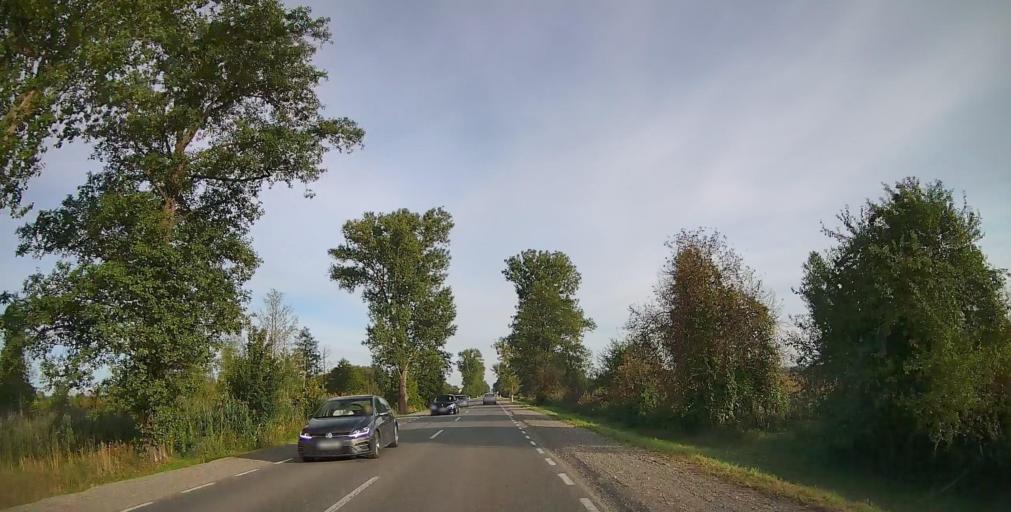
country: PL
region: Masovian Voivodeship
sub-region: Powiat piaseczynski
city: Baniocha
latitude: 52.0353
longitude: 21.0987
